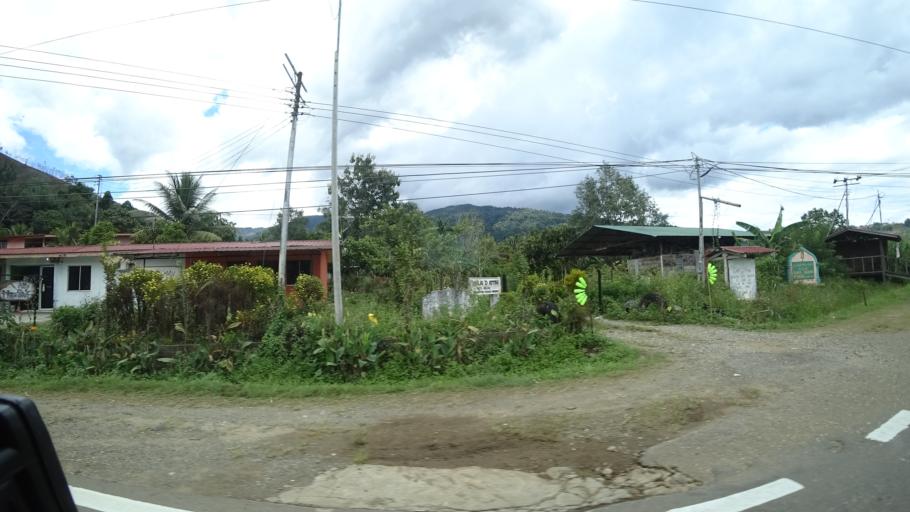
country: MY
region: Sabah
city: Ranau
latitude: 5.9939
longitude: 116.6976
